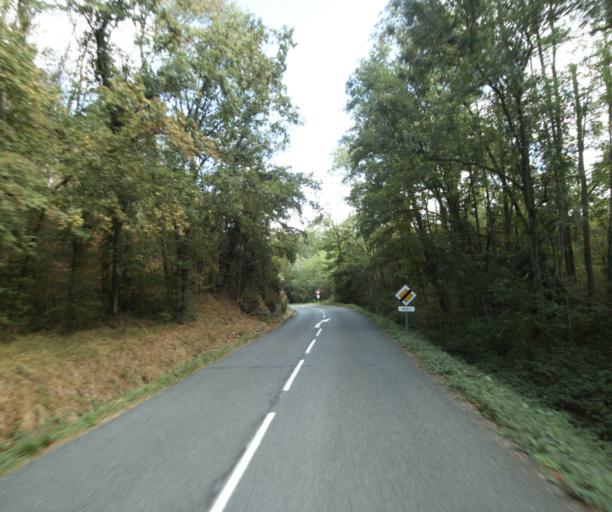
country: FR
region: Rhone-Alpes
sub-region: Departement du Rhone
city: Saint-Germain-Nuelles
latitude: 45.8522
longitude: 4.6433
